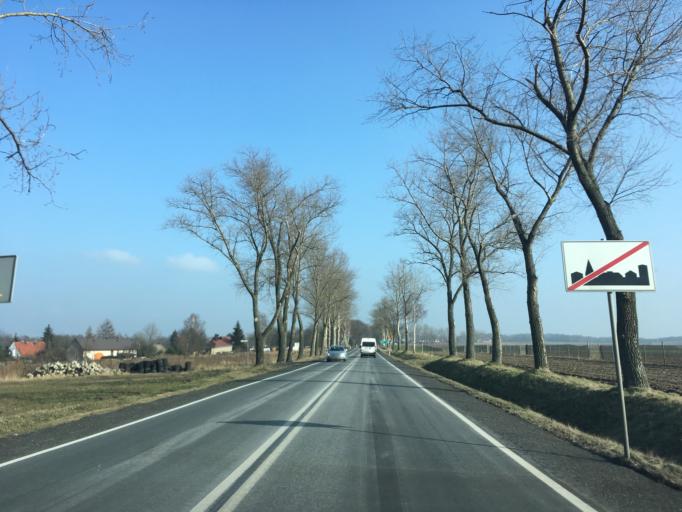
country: PL
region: Lower Silesian Voivodeship
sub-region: Powiat zlotoryjski
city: Olszanica
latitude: 51.2775
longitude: 15.8222
